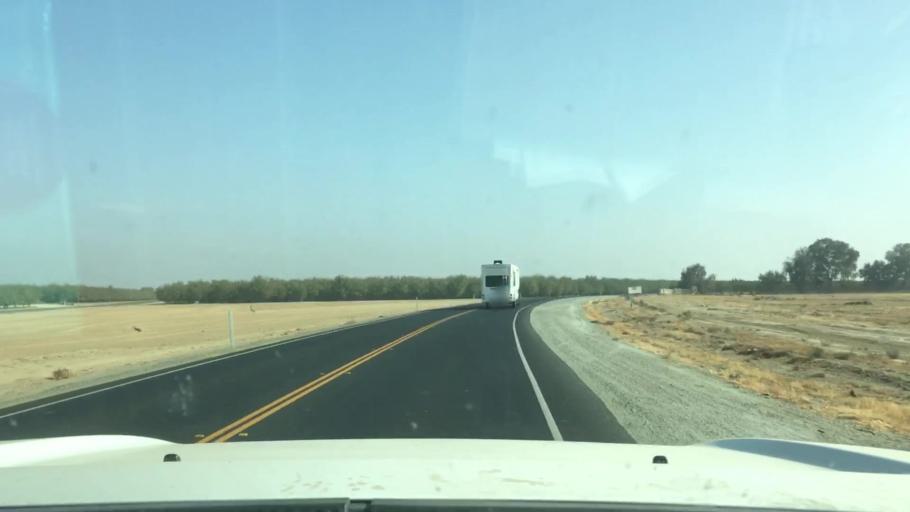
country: US
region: California
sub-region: Kern County
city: Lost Hills
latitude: 35.6155
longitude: -119.5918
